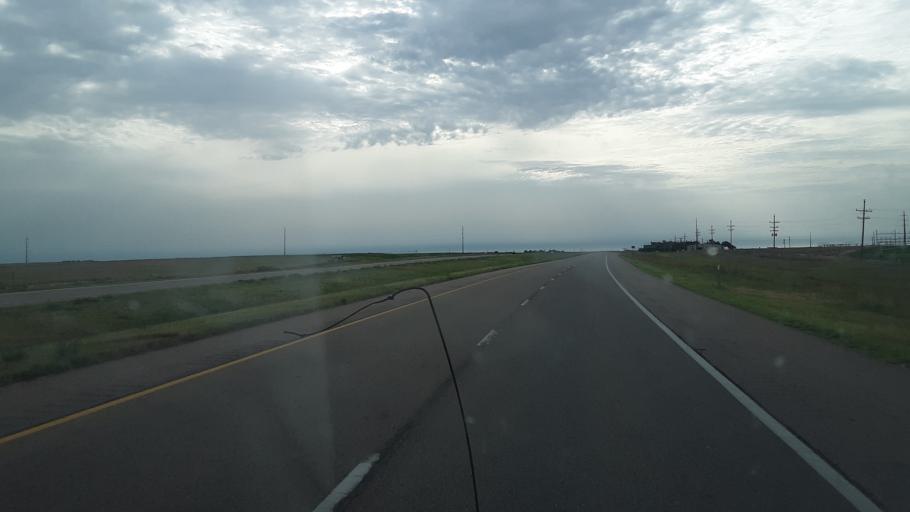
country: US
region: Kansas
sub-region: Finney County
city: Garden City
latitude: 37.9605
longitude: -100.7808
